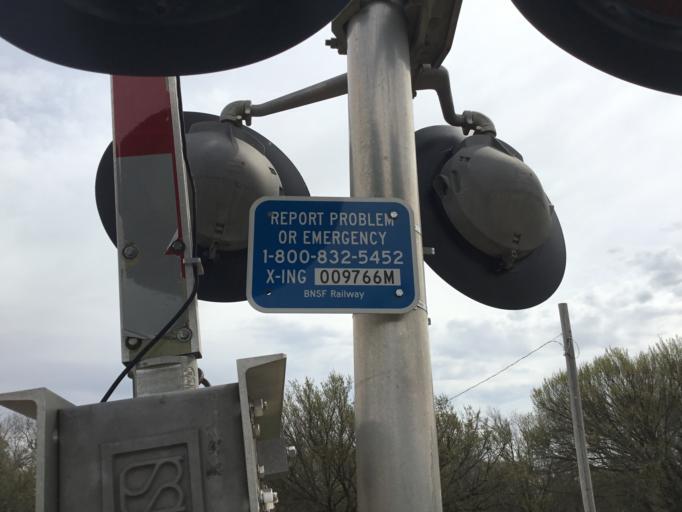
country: US
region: Kansas
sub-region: Butler County
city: Douglass
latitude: 37.5140
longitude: -97.0117
